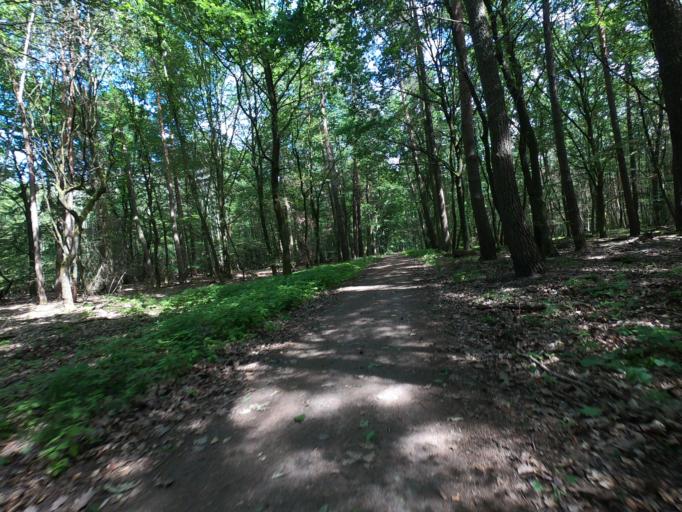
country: DE
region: Hesse
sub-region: Regierungsbezirk Darmstadt
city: Dietzenbach
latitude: 50.0255
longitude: 8.7621
